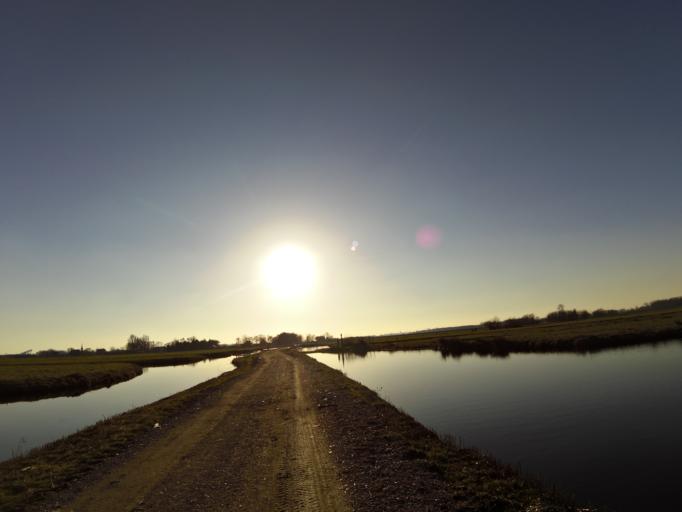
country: NL
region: South Holland
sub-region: Gemeente Voorschoten
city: Voorschoten
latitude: 52.1073
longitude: 4.4720
